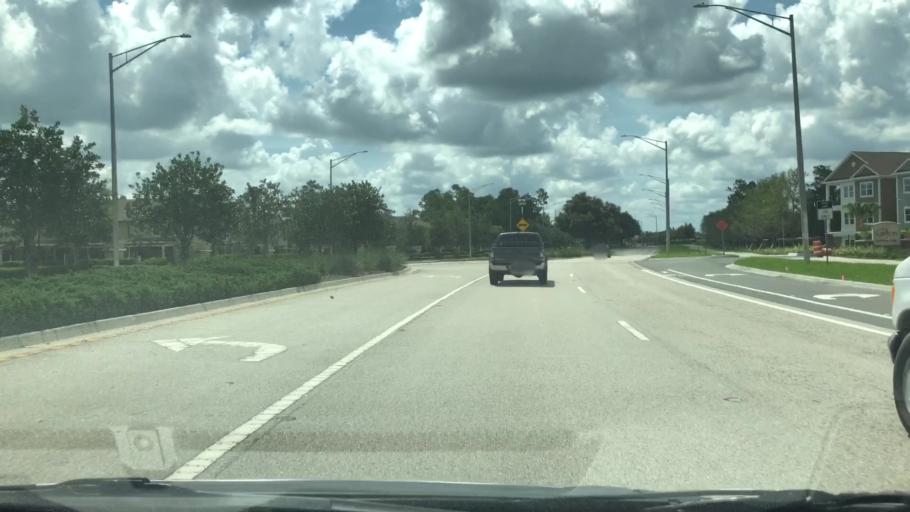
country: US
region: Florida
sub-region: Saint Johns County
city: Fruit Cove
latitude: 30.1196
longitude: -81.5229
